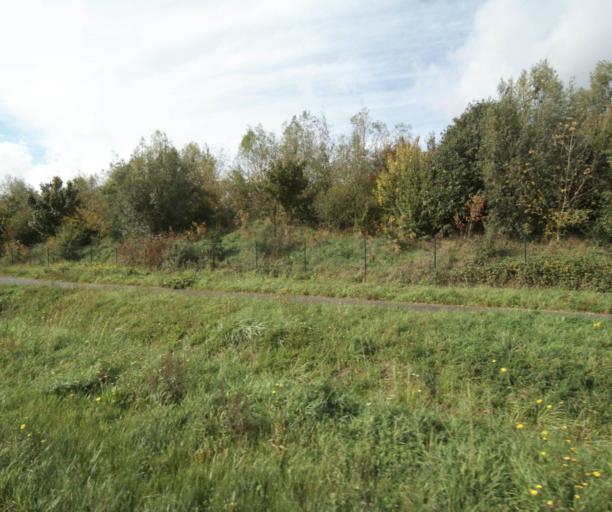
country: FR
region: Nord-Pas-de-Calais
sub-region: Departement du Nord
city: Houplines
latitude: 50.6803
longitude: 2.9142
